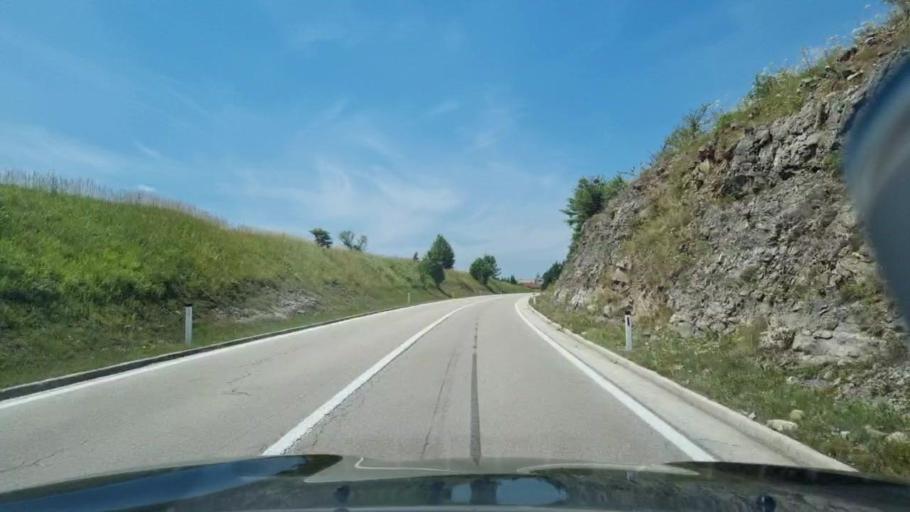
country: BA
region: Federation of Bosnia and Herzegovina
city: Sanica
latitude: 44.5478
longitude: 16.5869
